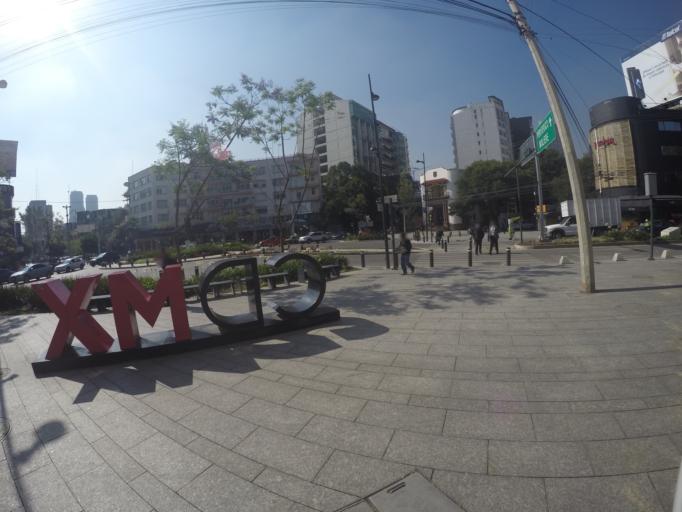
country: MX
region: Mexico City
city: Miguel Hidalgo
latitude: 19.4381
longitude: -99.2000
